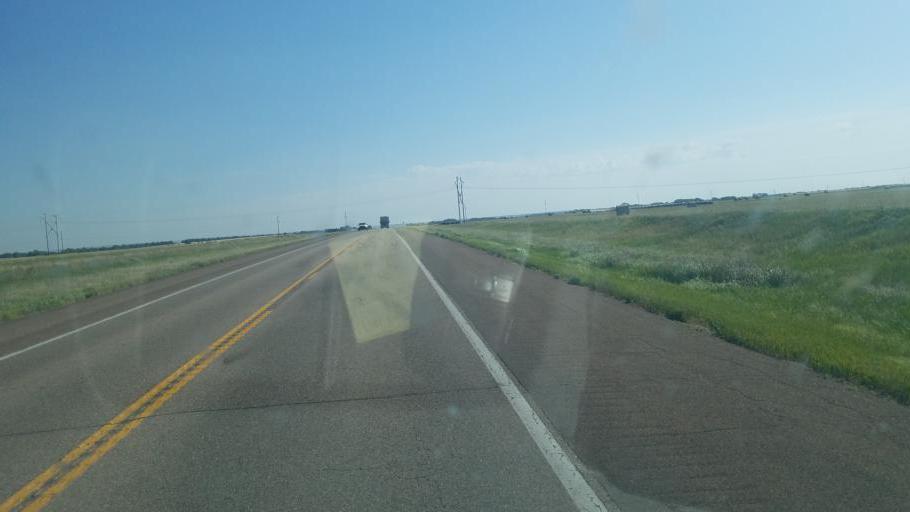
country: US
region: Kansas
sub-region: Barton County
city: Great Bend
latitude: 38.3867
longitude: -98.6796
